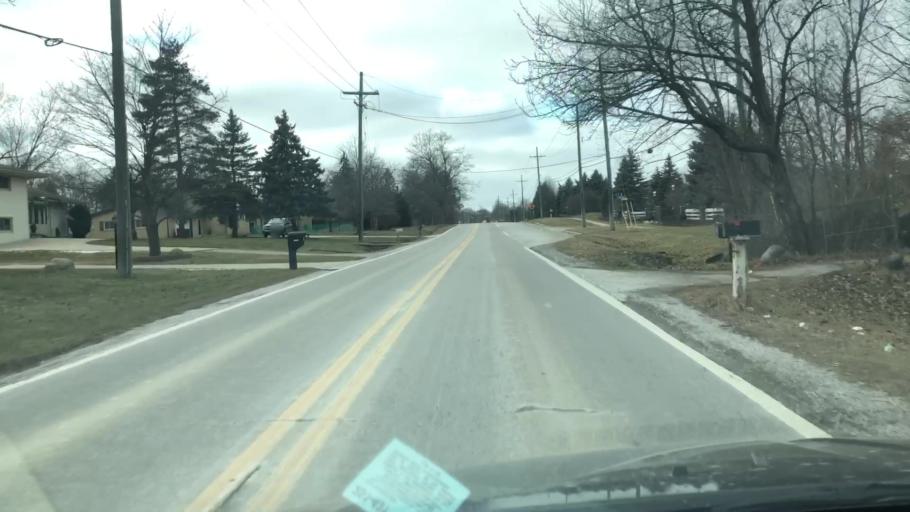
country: US
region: Michigan
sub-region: Macomb County
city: Romeo
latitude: 42.7430
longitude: -83.0318
